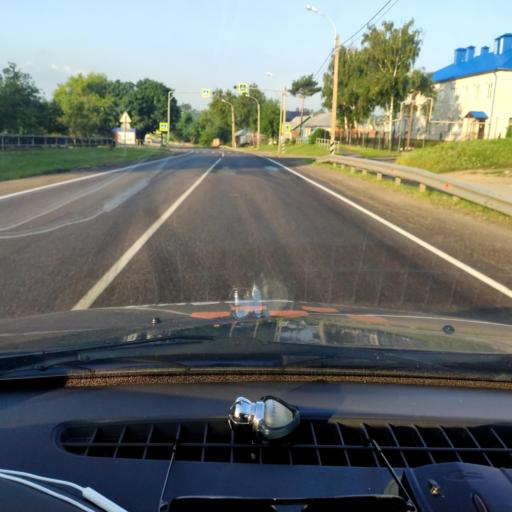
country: RU
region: Lipetsk
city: Kazaki
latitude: 52.6282
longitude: 38.2738
